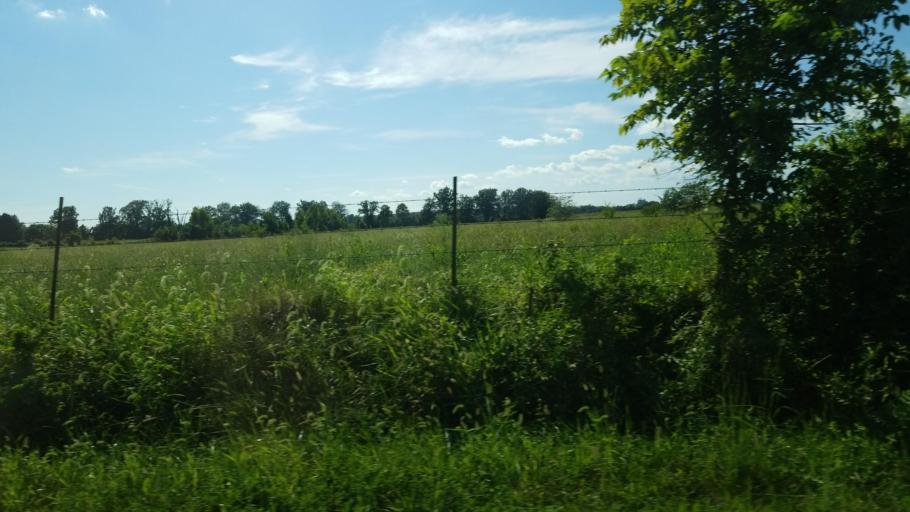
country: US
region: Illinois
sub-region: Saline County
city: Harrisburg
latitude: 37.8197
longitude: -88.5487
